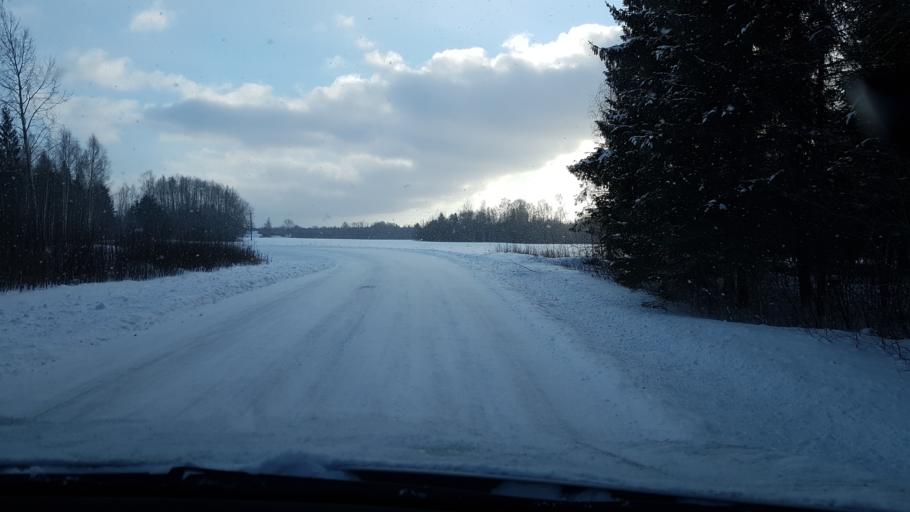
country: EE
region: Harju
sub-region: Nissi vald
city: Turba
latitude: 59.1704
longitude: 24.1375
